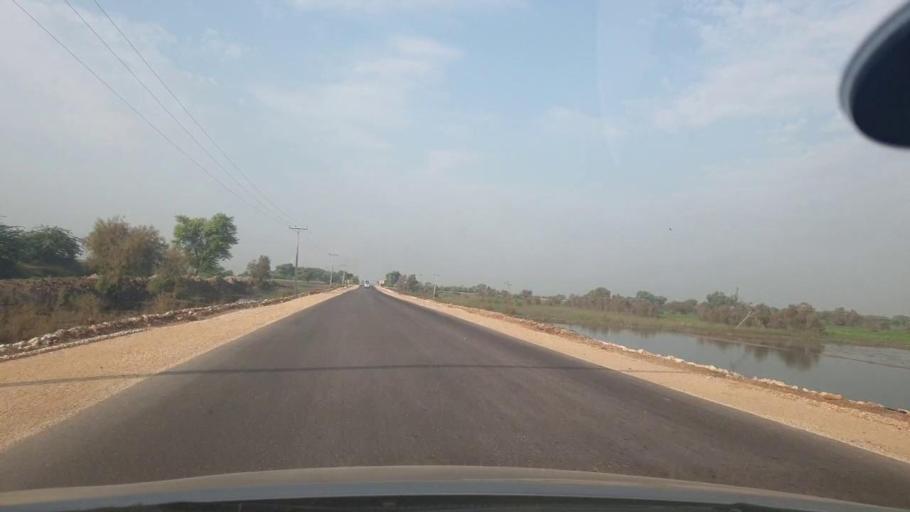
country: PK
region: Sindh
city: Jacobabad
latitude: 28.2373
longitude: 68.3907
